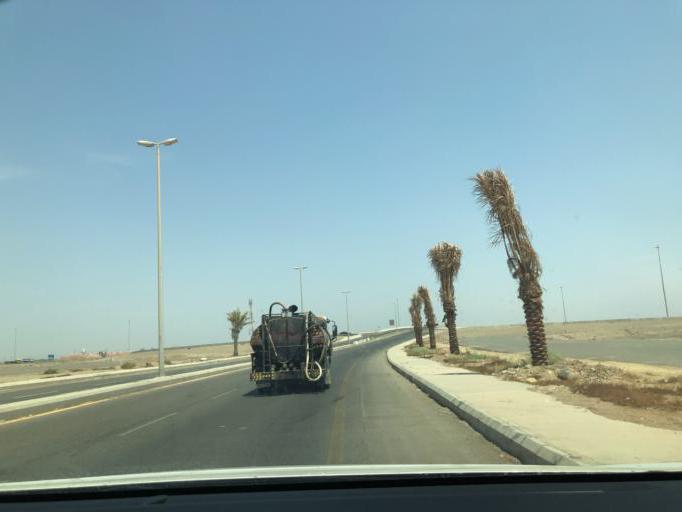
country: SA
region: Makkah
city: Rabigh
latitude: 22.2753
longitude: 39.1224
